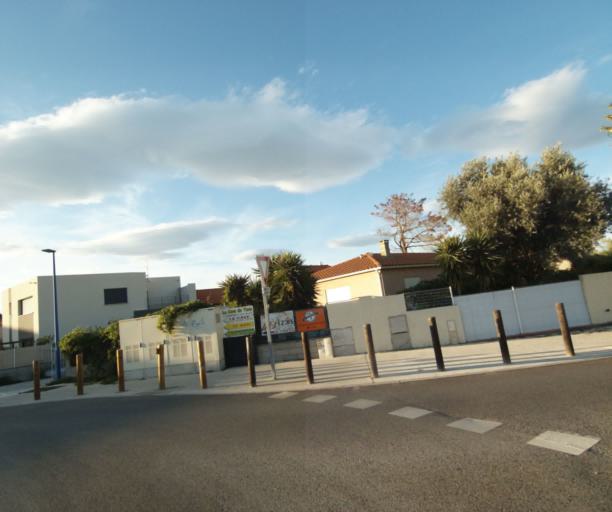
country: FR
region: Languedoc-Roussillon
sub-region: Departement des Pyrenees-Orientales
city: Argelers
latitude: 42.5673
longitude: 3.0057
